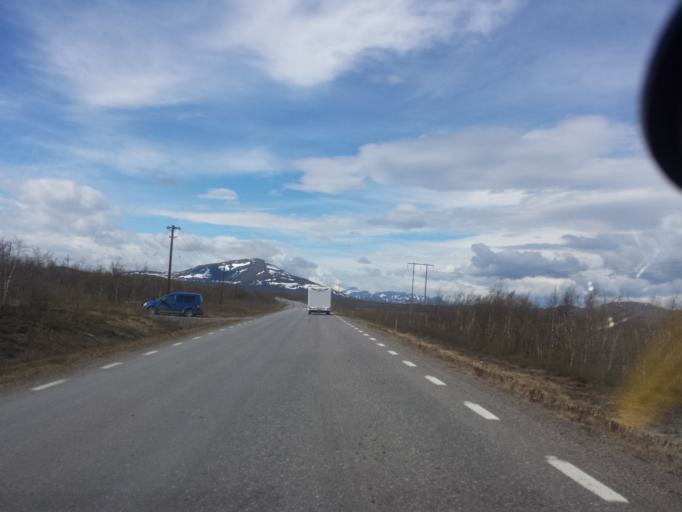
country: SE
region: Norrbotten
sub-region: Kiruna Kommun
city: Kiruna
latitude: 68.1079
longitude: 19.8379
